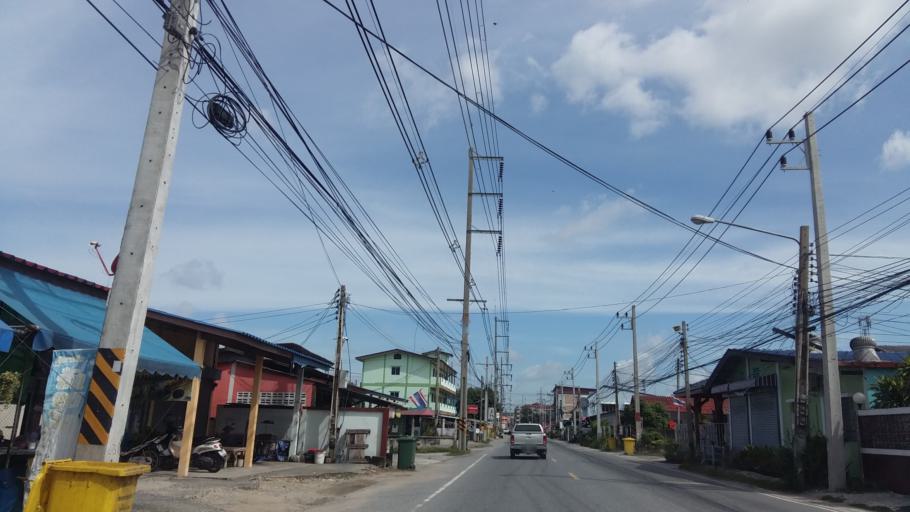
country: TH
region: Chon Buri
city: Phan Thong
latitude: 13.4350
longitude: 101.0615
